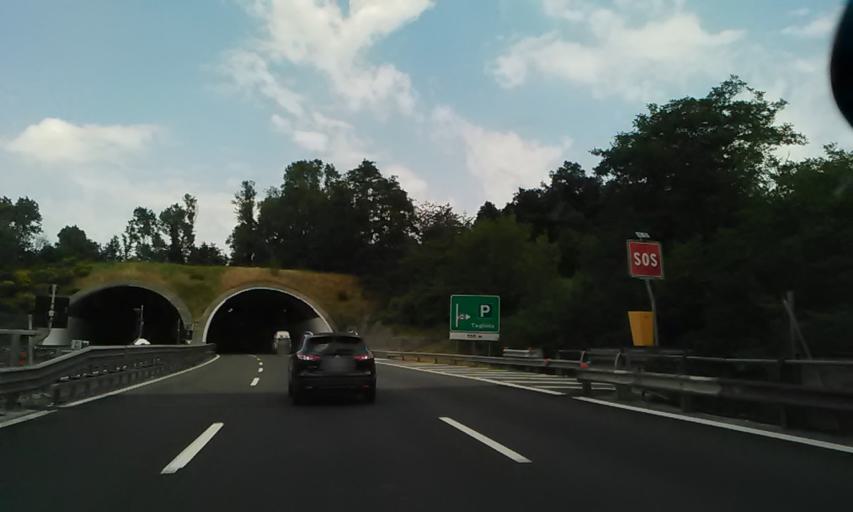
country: IT
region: Piedmont
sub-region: Provincia di Alessandria
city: Tagliolo Monferrato
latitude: 44.6347
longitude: 8.6630
